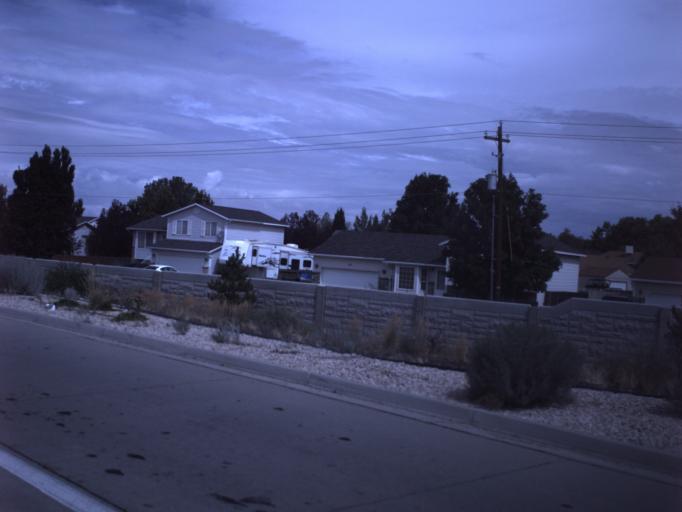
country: US
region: Utah
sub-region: Davis County
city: Clearfield
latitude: 41.1106
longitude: -112.0336
